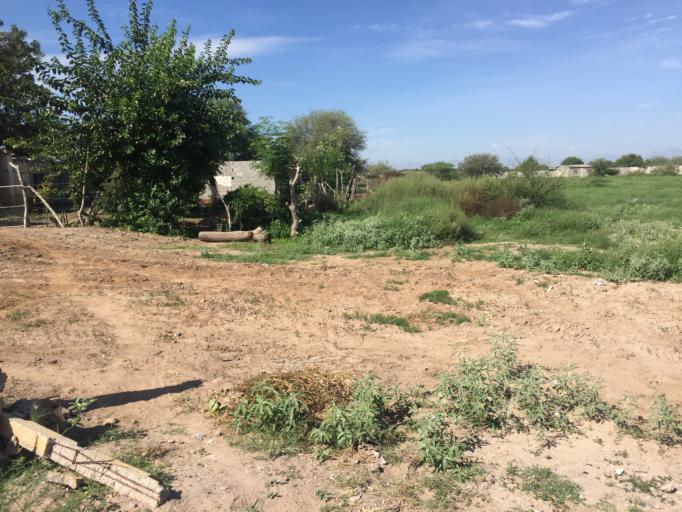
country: MX
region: Coahuila
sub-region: Matamoros
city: Veinte de Noviembre
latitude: 25.7202
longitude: -103.3520
